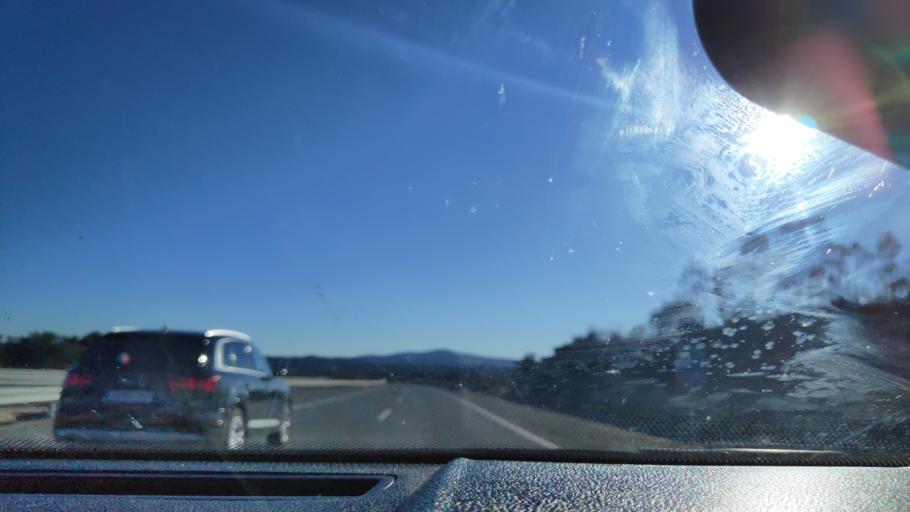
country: ES
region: Extremadura
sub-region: Provincia de Badajoz
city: Monesterio
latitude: 38.0034
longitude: -6.2324
